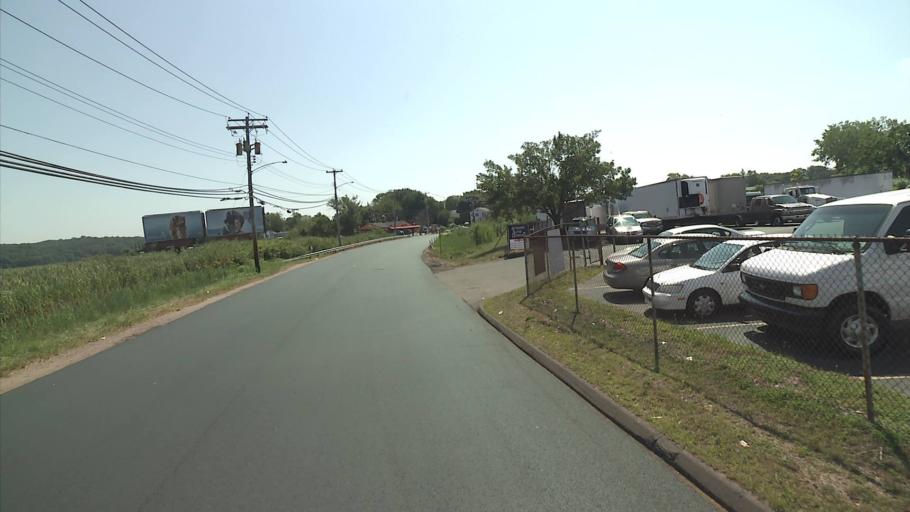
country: US
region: Connecticut
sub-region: New Haven County
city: East Haven
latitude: 41.2662
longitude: -72.8714
